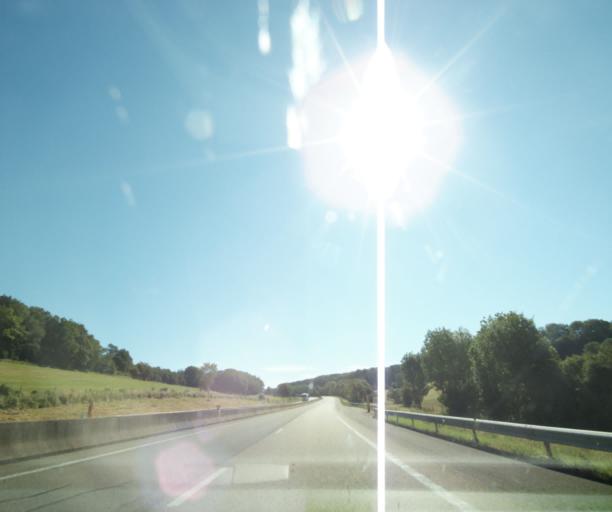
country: FR
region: Champagne-Ardenne
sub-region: Departement de la Haute-Marne
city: Avrecourt
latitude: 47.9593
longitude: 5.4532
